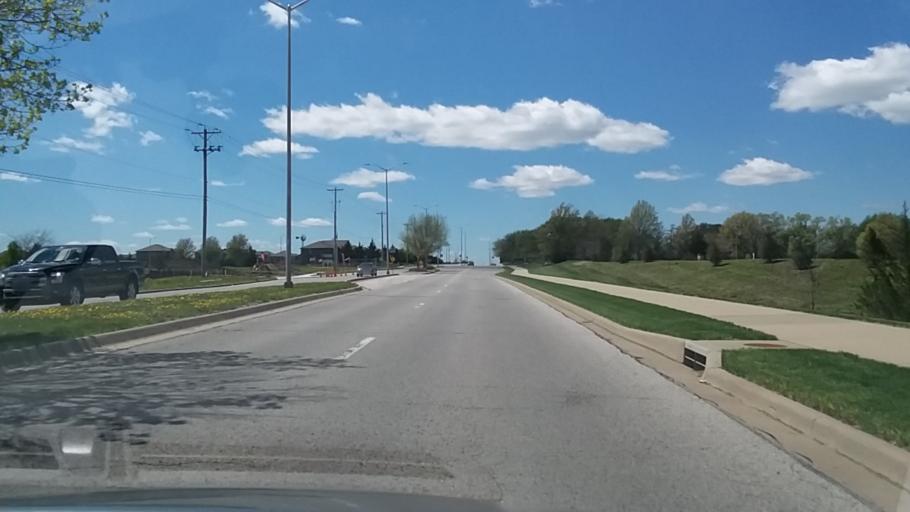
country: US
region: Kansas
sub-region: Johnson County
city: Olathe
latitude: 38.8839
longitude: -94.8543
